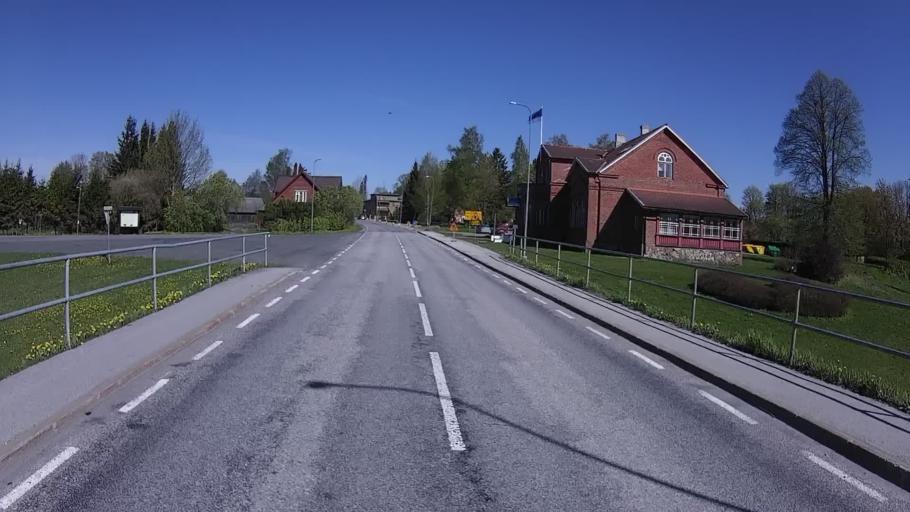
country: EE
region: Paernumaa
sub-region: Tootsi vald
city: Tootsi
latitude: 58.4850
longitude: 24.8143
